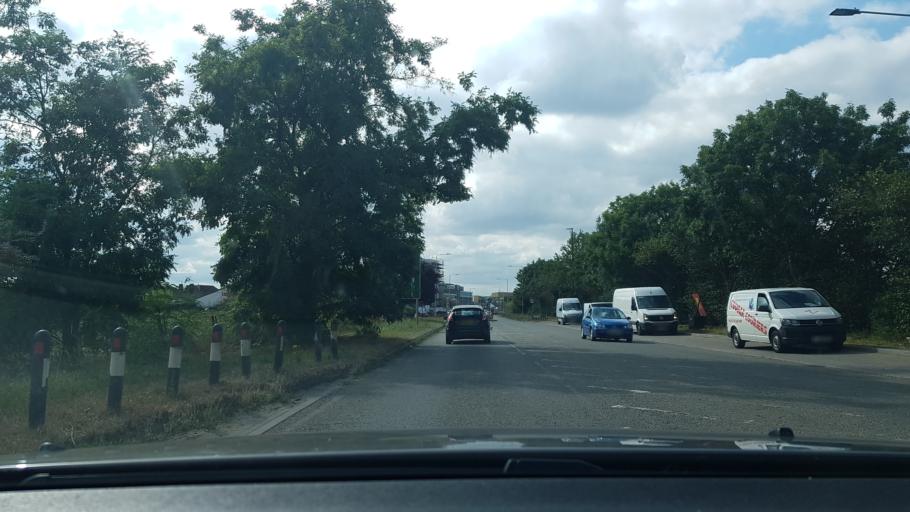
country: GB
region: England
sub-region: Surrey
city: Colnbrook
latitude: 51.4880
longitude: -0.5298
